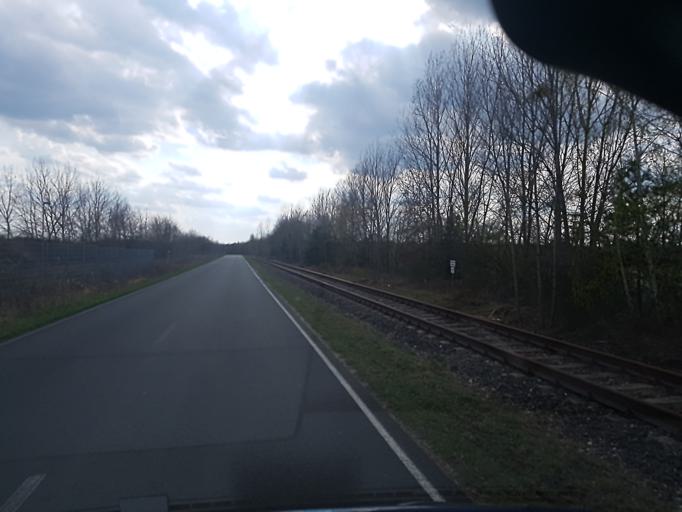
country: DE
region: Saxony-Anhalt
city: Grafenhainichen
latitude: 51.7569
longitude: 12.4422
